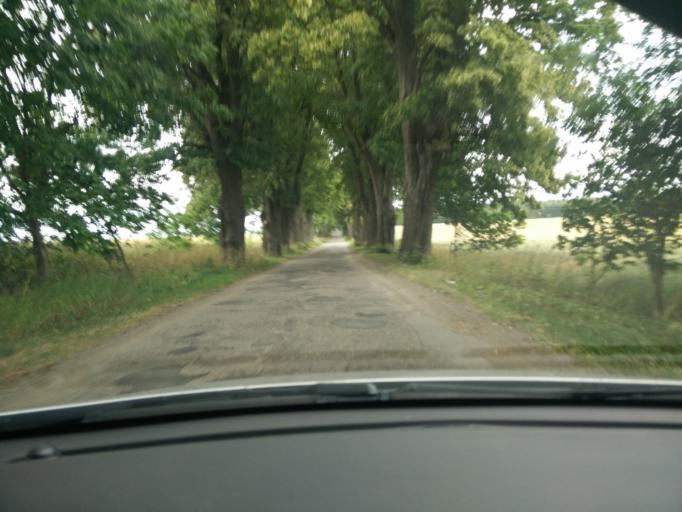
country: PL
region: Pomeranian Voivodeship
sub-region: Powiat pucki
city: Mrzezino
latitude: 54.6712
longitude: 18.4576
